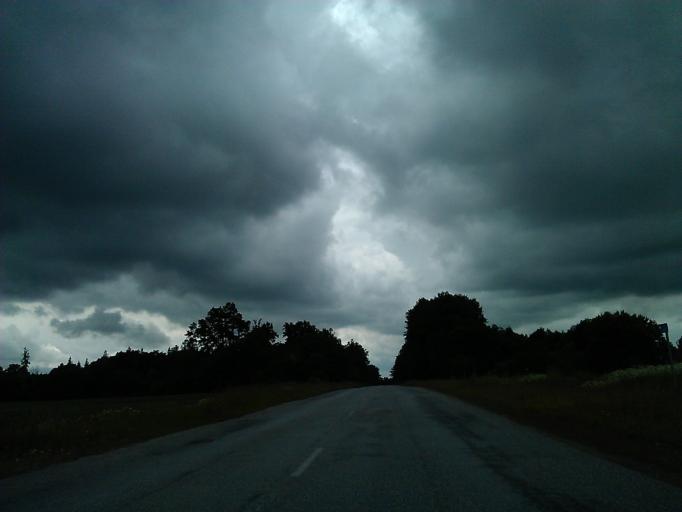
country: LV
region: Aizpute
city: Aizpute
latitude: 56.8180
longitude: 21.7264
